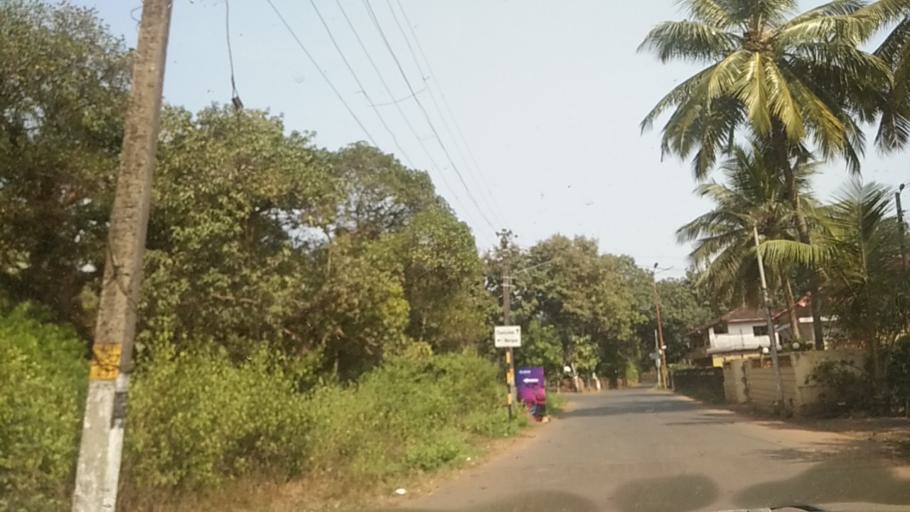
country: IN
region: Goa
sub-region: South Goa
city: Cavelossim
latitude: 15.1517
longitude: 73.9643
